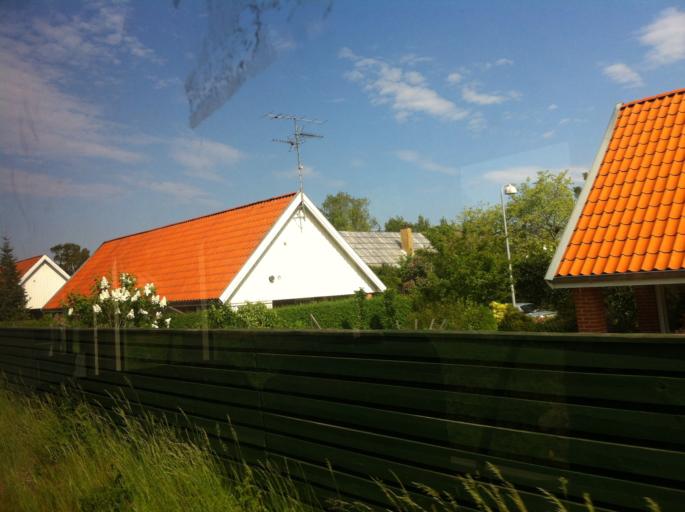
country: DK
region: Capital Region
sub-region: Helsingor Kommune
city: Hornbaek
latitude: 56.0975
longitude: 12.3899
